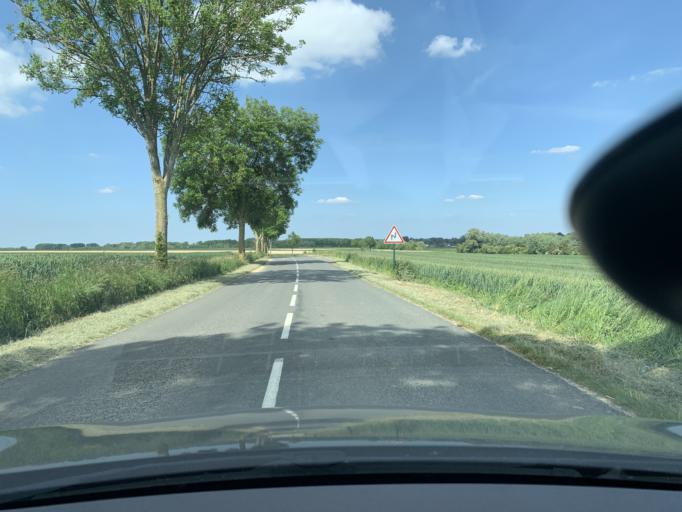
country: FR
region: Nord-Pas-de-Calais
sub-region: Departement du Pas-de-Calais
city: Marquion
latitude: 50.2280
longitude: 3.0836
